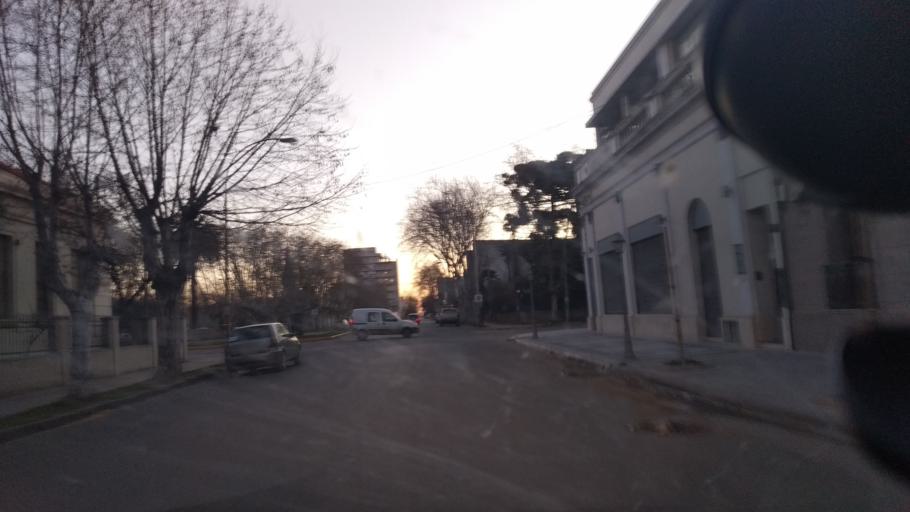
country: AR
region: Buenos Aires
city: Necochea
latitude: -38.5525
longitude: -58.7390
